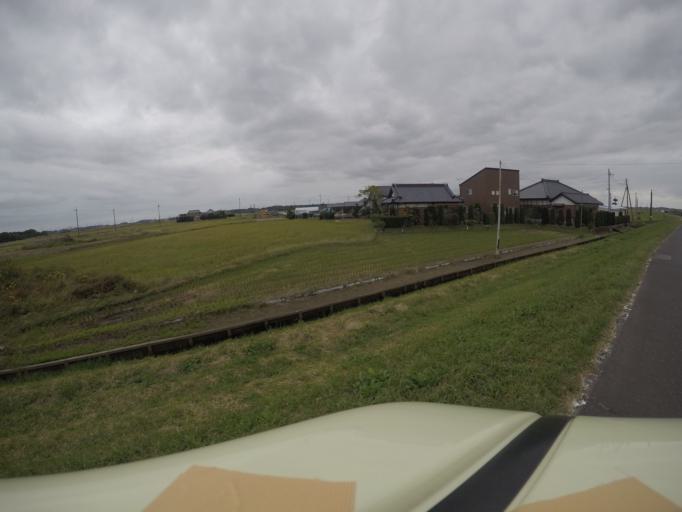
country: JP
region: Ibaraki
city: Inashiki
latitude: 35.9849
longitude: 140.4201
